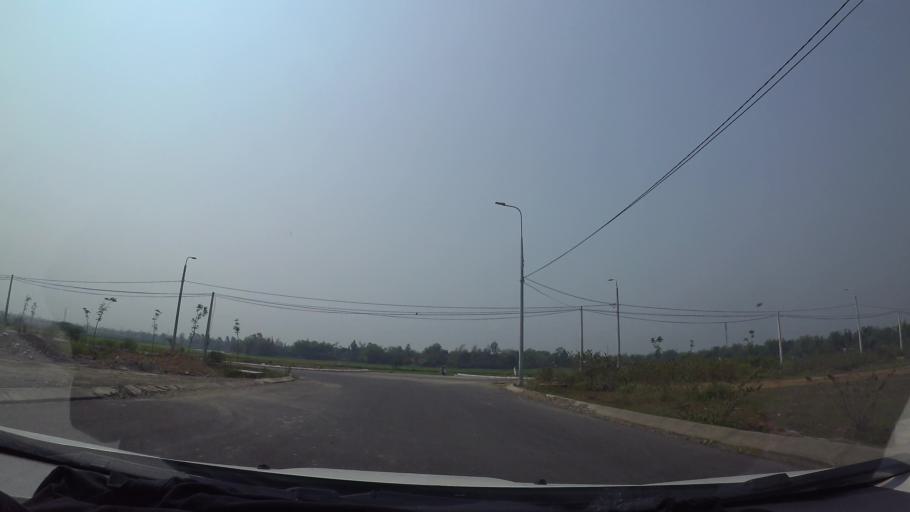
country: VN
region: Da Nang
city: Cam Le
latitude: 15.9813
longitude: 108.2272
